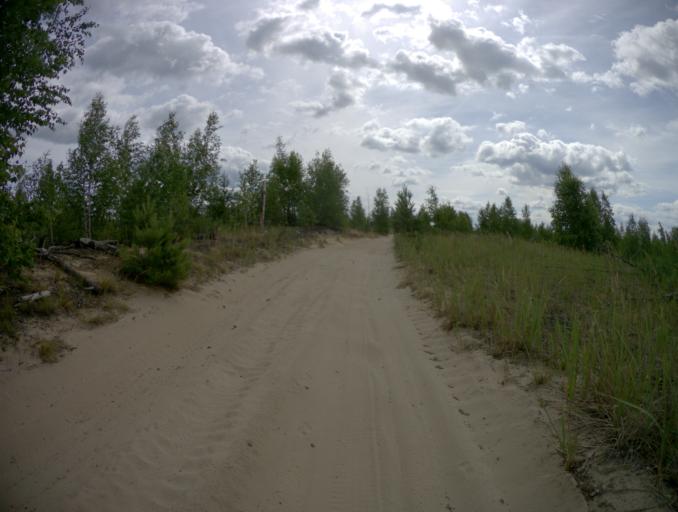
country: RU
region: Nizjnij Novgorod
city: Frolishchi
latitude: 56.5032
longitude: 42.5352
